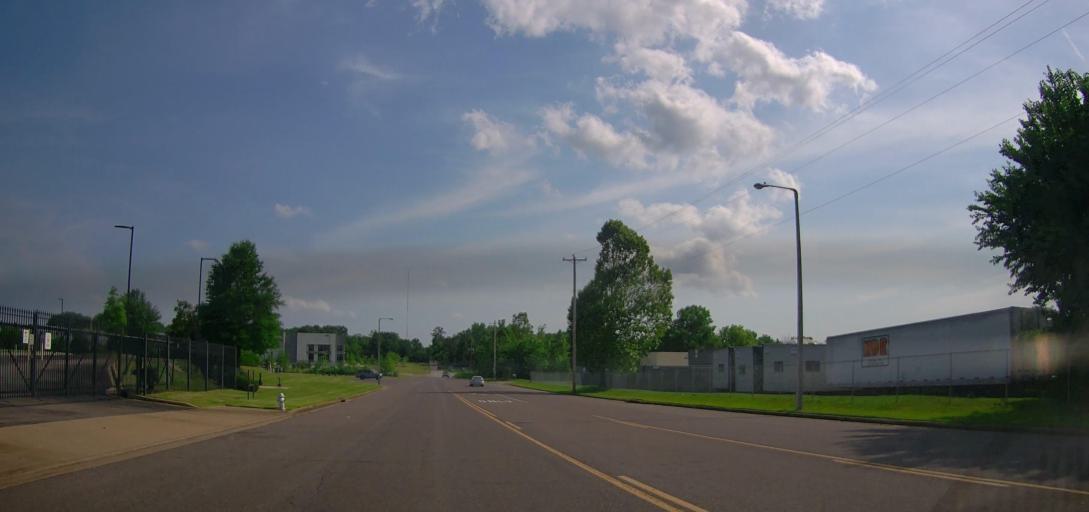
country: US
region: Mississippi
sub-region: De Soto County
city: Olive Branch
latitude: 34.9983
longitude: -89.8607
